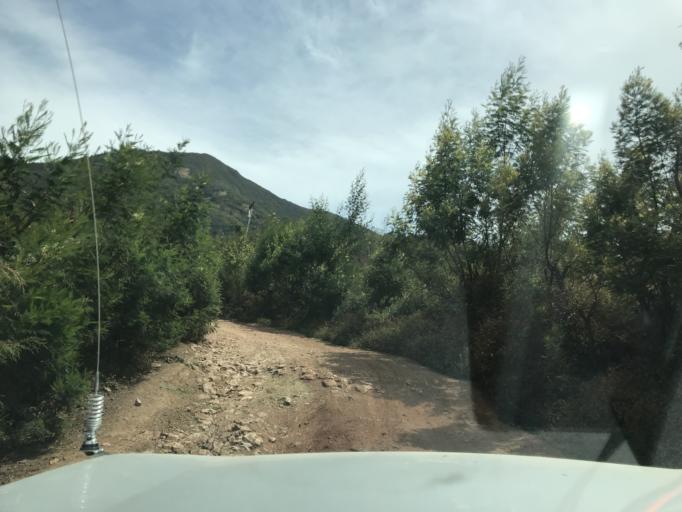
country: TL
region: Ainaro
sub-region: Ainaro
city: Ainaro
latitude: -8.8834
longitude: 125.5334
